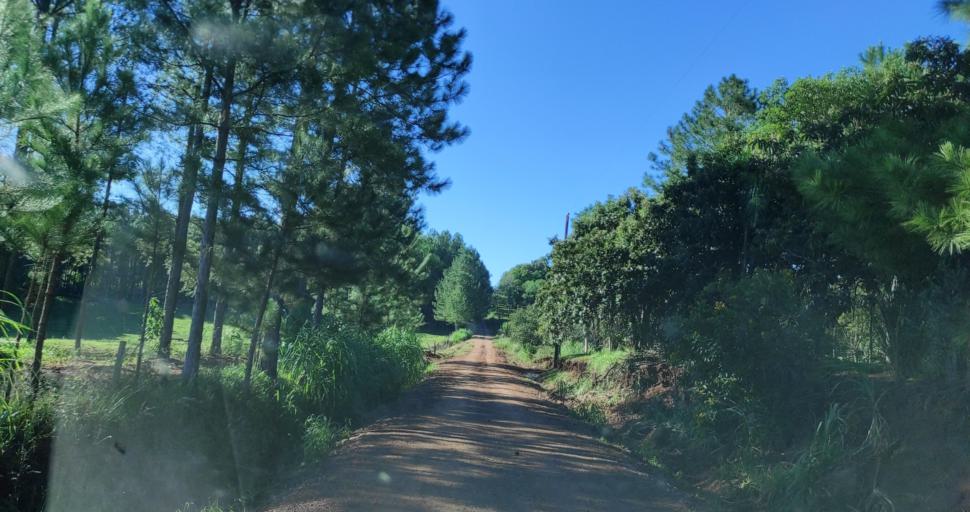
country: AR
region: Misiones
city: Capiovi
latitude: -26.9227
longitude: -55.0004
